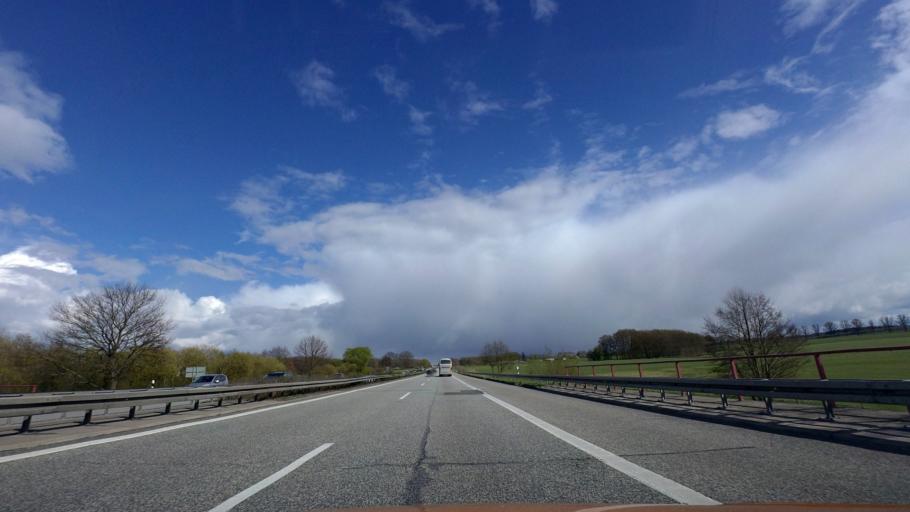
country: DE
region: Mecklenburg-Vorpommern
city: Wittenburg
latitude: 53.5014
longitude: 11.0486
